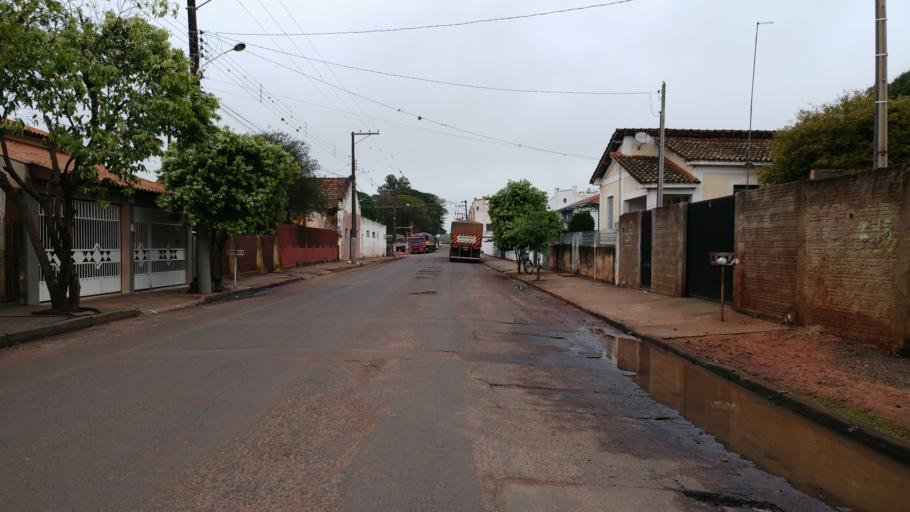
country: BR
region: Sao Paulo
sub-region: Paraguacu Paulista
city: Paraguacu Paulista
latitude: -22.4195
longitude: -50.5724
